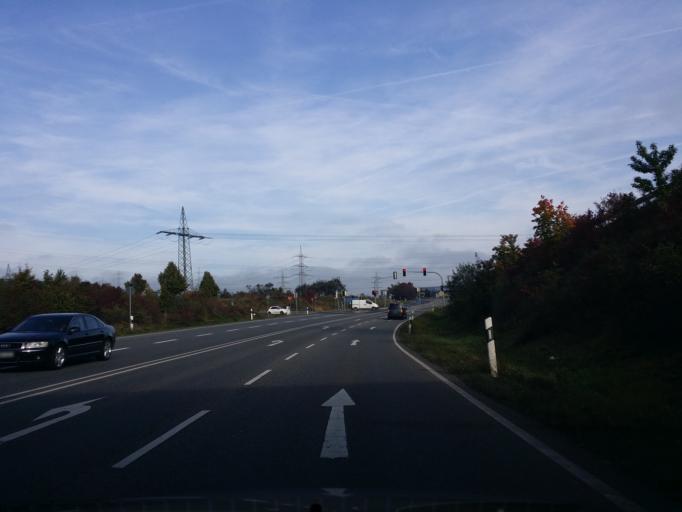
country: DE
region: Hesse
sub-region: Regierungsbezirk Darmstadt
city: Hofheim am Taunus
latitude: 50.0557
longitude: 8.4332
